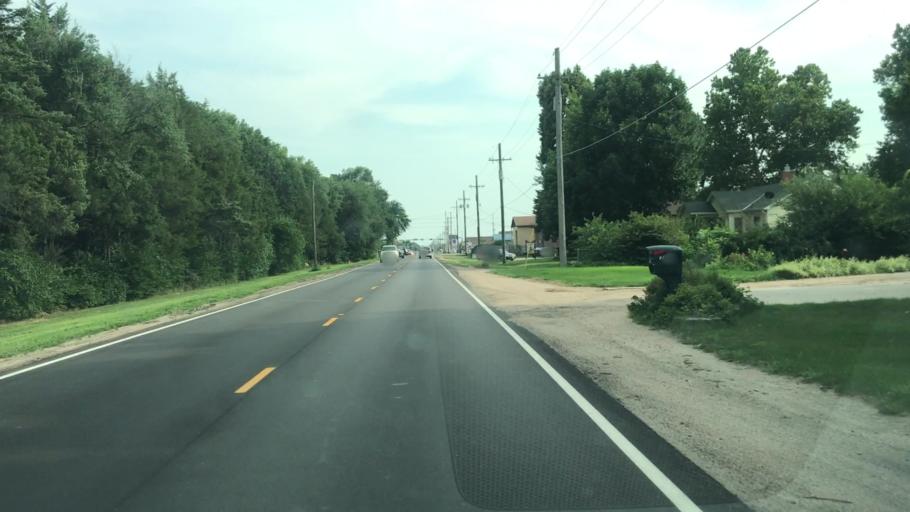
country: US
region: Nebraska
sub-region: Hall County
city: Grand Island
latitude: 40.9490
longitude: -98.3788
